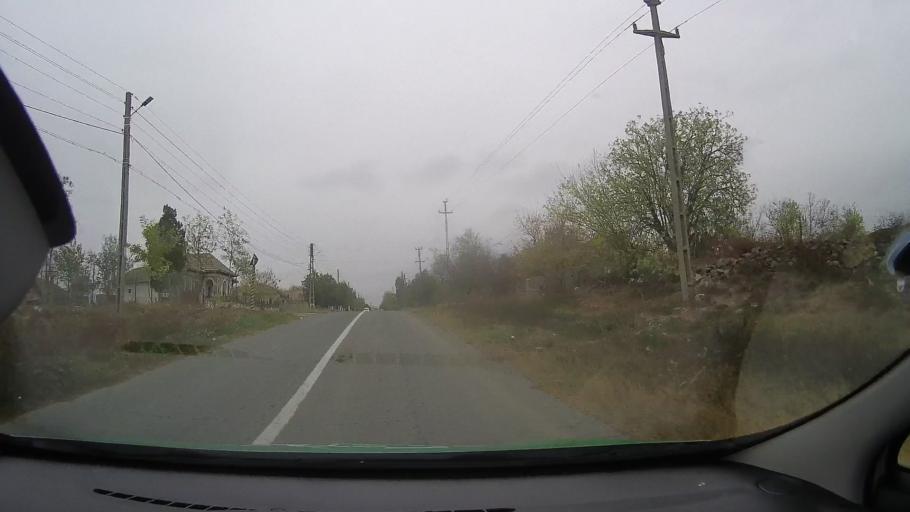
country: RO
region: Constanta
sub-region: Comuna Pantelimon
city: Pantelimon
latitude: 44.5434
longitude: 28.3291
